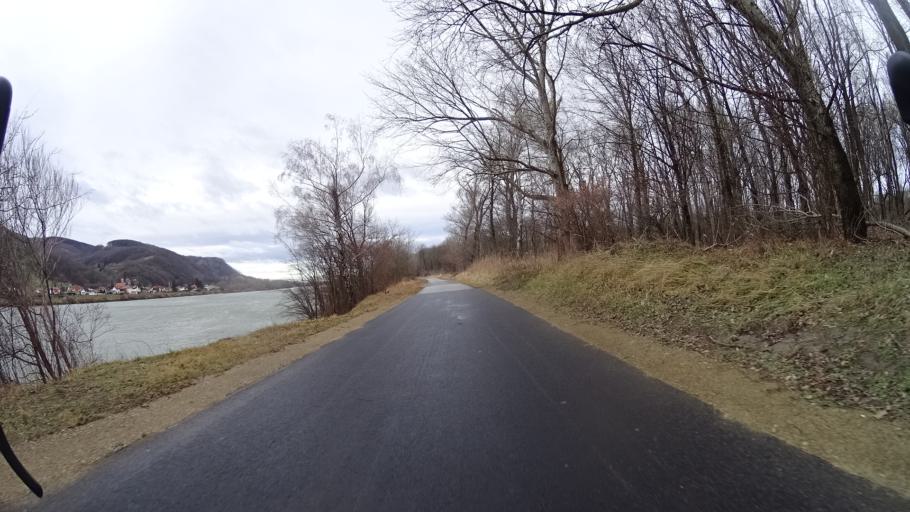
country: AT
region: Lower Austria
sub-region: Politischer Bezirk Korneuburg
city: Leobendorf
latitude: 48.3537
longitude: 16.2836
